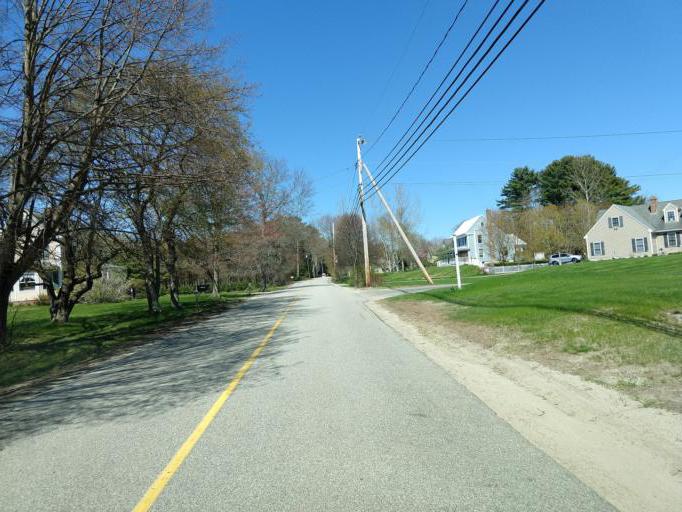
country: US
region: Maine
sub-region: York County
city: Arundel
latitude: 43.3759
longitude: -70.4743
